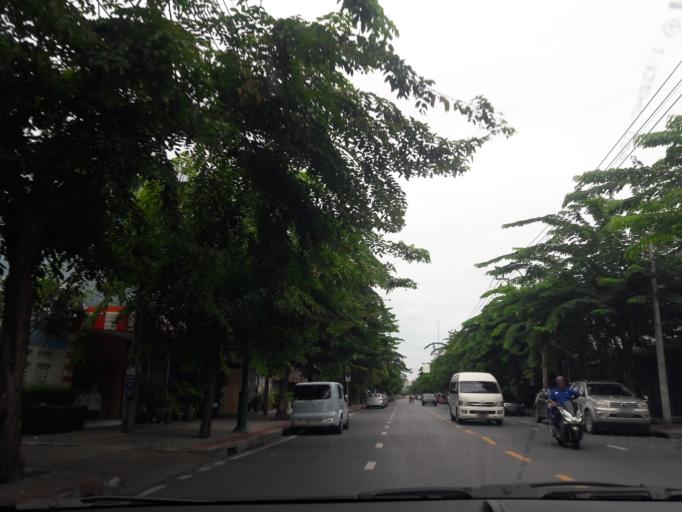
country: TH
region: Bangkok
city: Thon Buri
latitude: 13.7302
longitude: 100.4965
